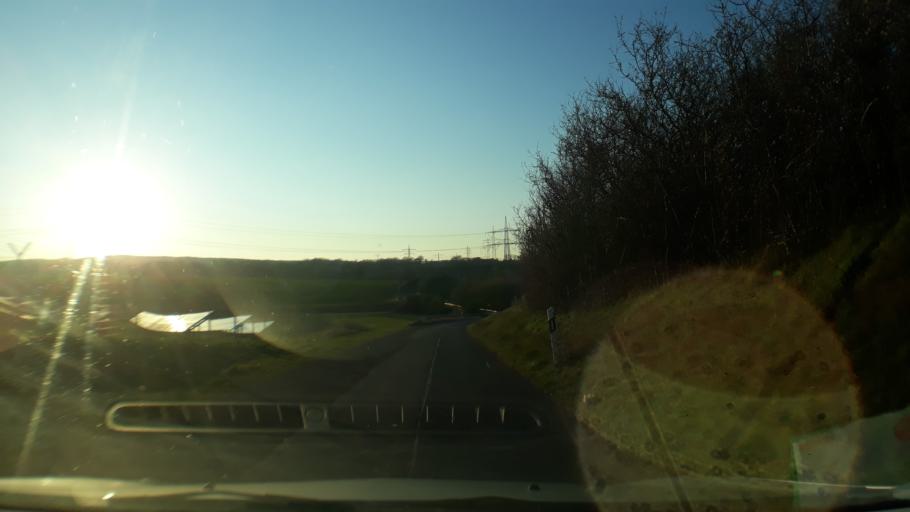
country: DE
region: North Rhine-Westphalia
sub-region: Regierungsbezirk Koln
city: Kall
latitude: 50.5715
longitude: 6.5990
